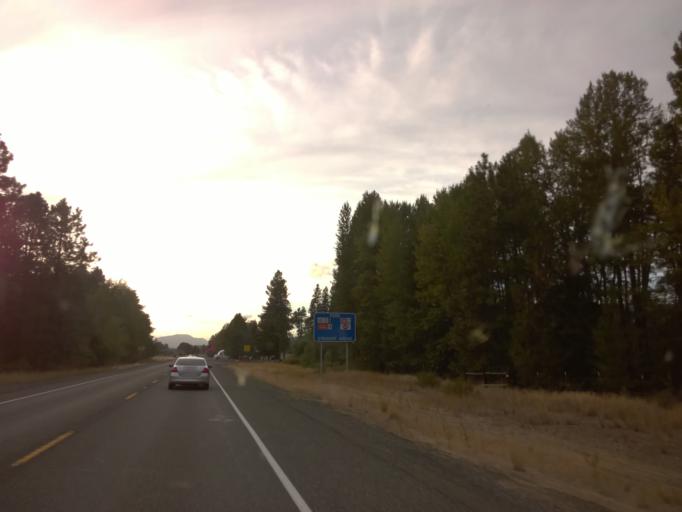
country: US
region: Washington
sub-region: Kittitas County
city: Cle Elum
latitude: 47.1840
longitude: -120.8883
